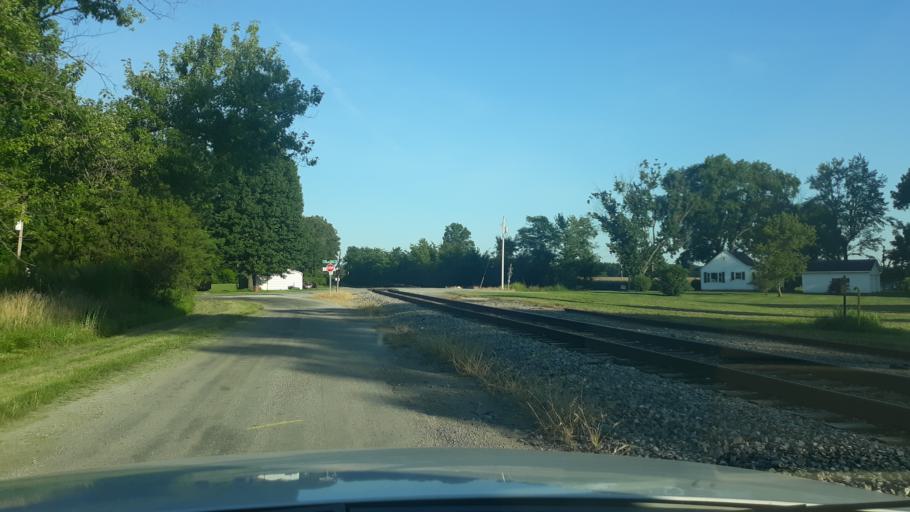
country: US
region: Illinois
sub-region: Saline County
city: Harrisburg
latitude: 37.8365
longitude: -88.6126
